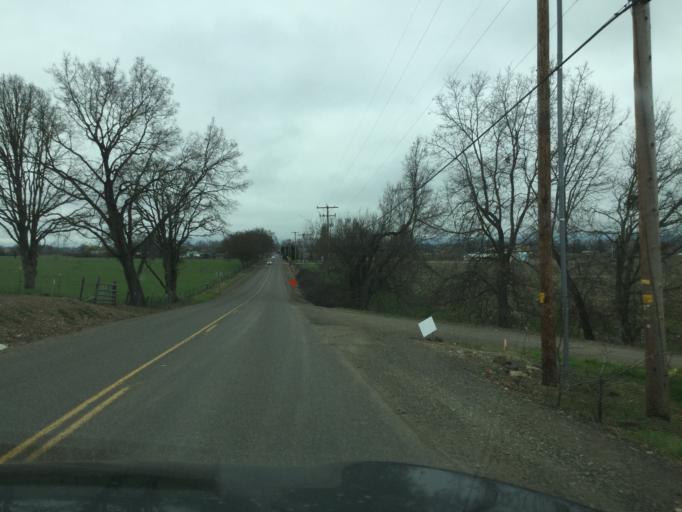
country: US
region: Oregon
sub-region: Jackson County
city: Central Point
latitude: 42.4009
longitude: -122.9094
